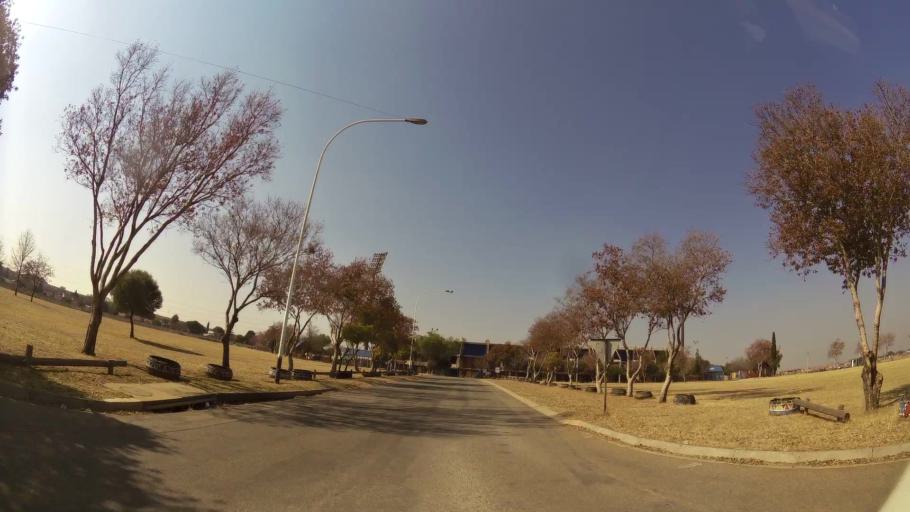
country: ZA
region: Gauteng
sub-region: Ekurhuleni Metropolitan Municipality
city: Boksburg
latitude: -26.2352
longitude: 28.2756
